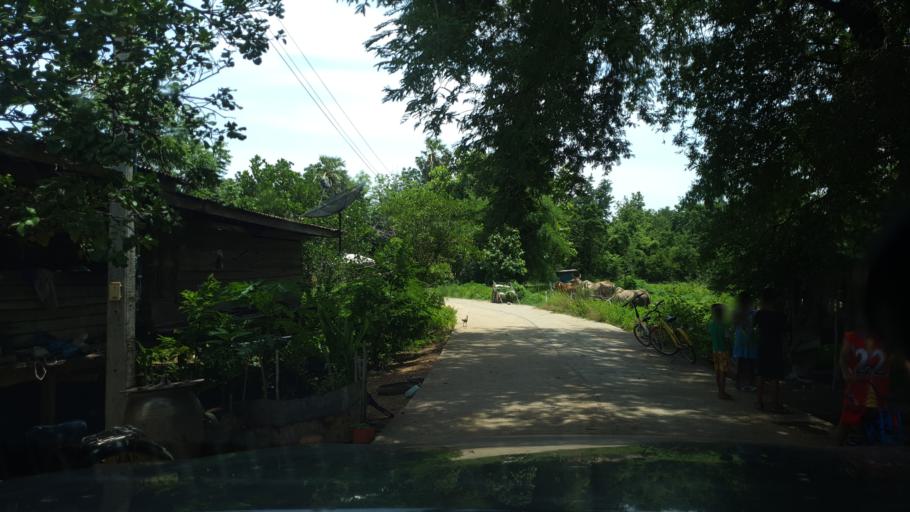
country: TH
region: Sukhothai
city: Ban Na
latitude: 17.0856
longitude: 99.6883
